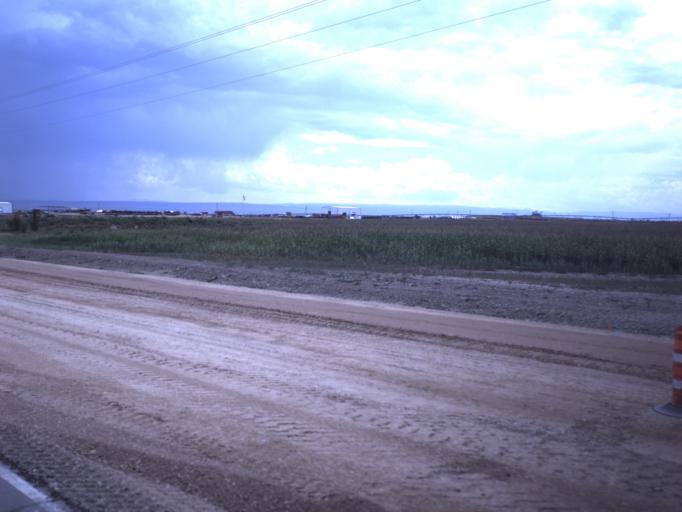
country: US
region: Utah
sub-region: Duchesne County
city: Roosevelt
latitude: 40.2233
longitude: -110.0674
